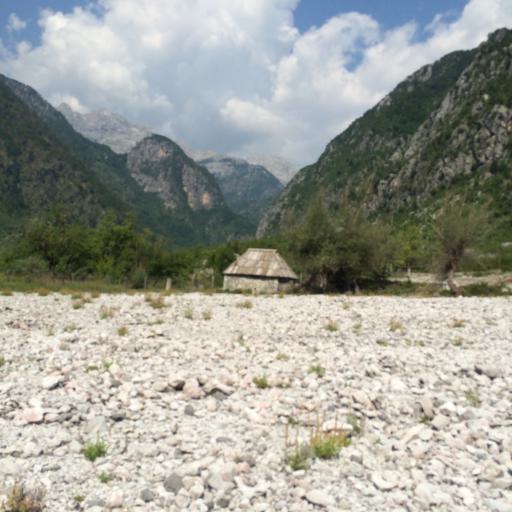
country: AL
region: Shkoder
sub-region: Rrethi i Shkodres
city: Nicaj-Shale
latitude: 42.3554
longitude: 19.7756
